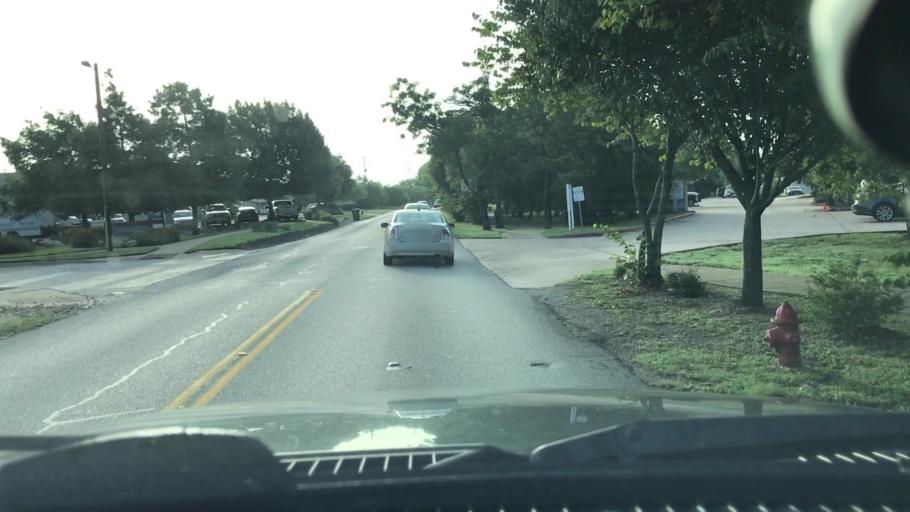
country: US
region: Texas
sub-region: Williamson County
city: Cedar Park
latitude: 30.5050
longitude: -97.8173
